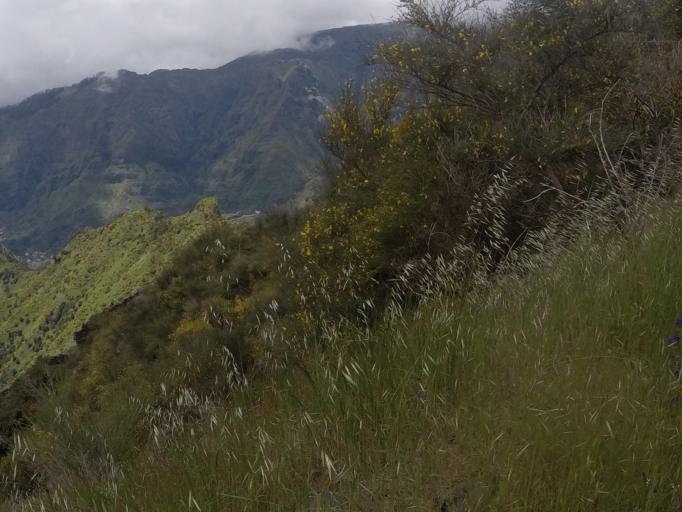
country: PT
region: Madeira
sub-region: Camara de Lobos
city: Curral das Freiras
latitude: 32.7400
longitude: -17.0048
